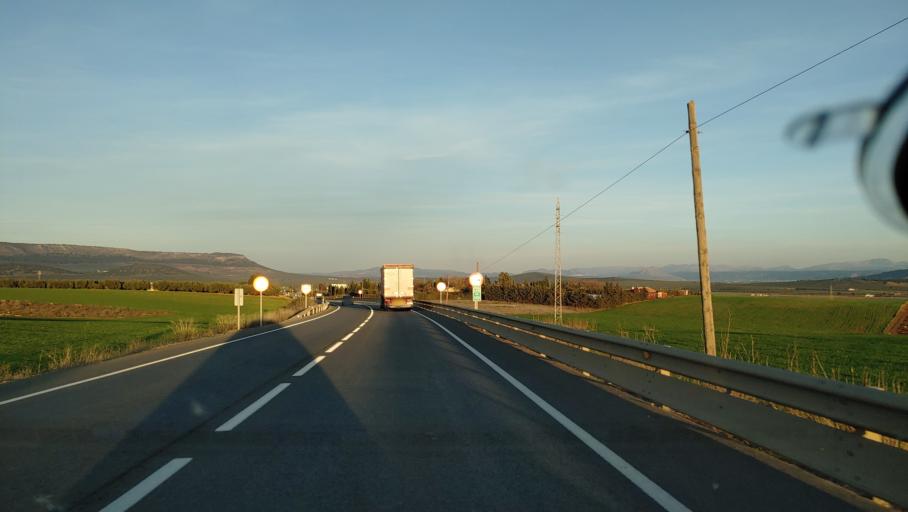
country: ES
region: Andalusia
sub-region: Provincia de Malaga
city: Humilladero
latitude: 37.0591
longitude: -4.7300
